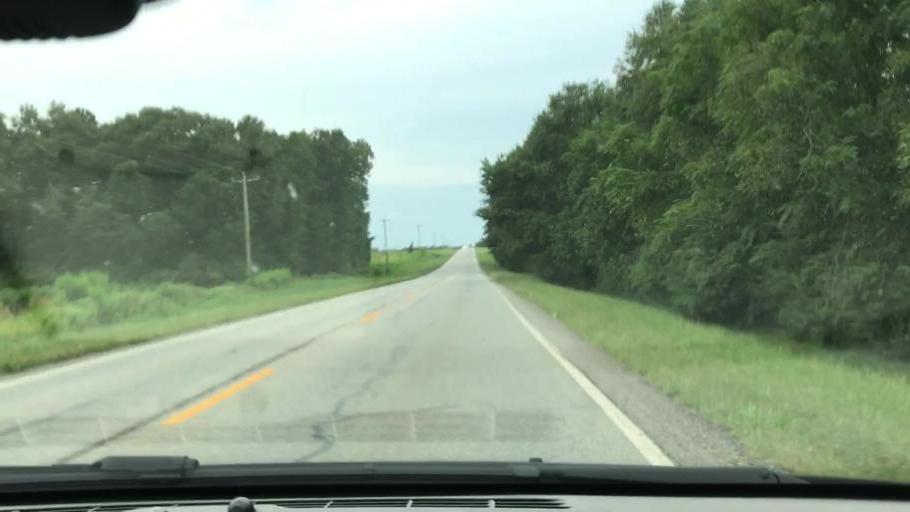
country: US
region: Georgia
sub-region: Early County
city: Blakely
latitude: 31.3586
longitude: -84.9692
